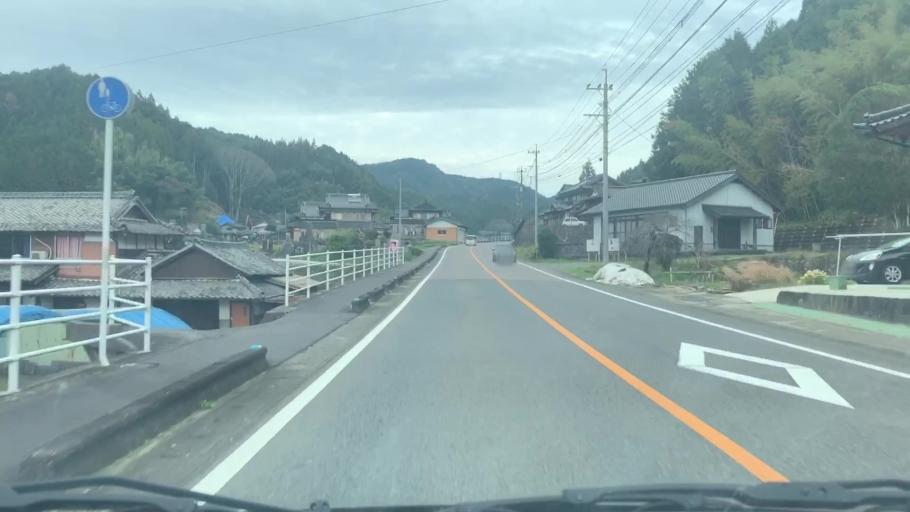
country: JP
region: Saga Prefecture
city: Ureshinomachi-shimojuku
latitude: 33.1524
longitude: 129.9735
